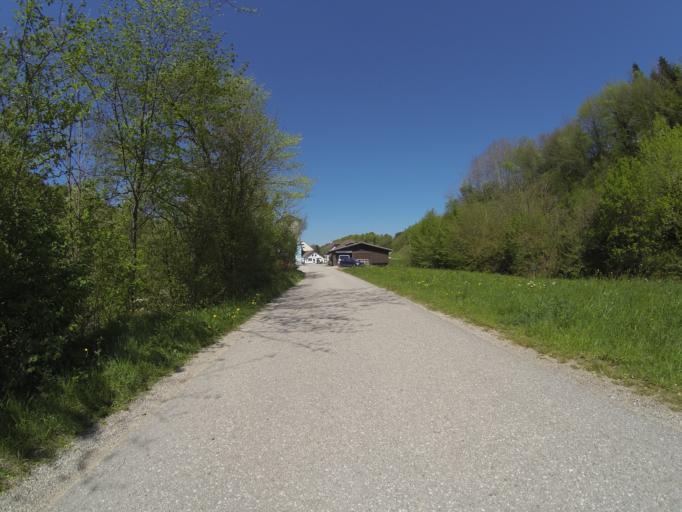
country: AT
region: Upper Austria
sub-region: Politischer Bezirk Gmunden
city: Altmunster
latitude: 47.9311
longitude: 13.7535
